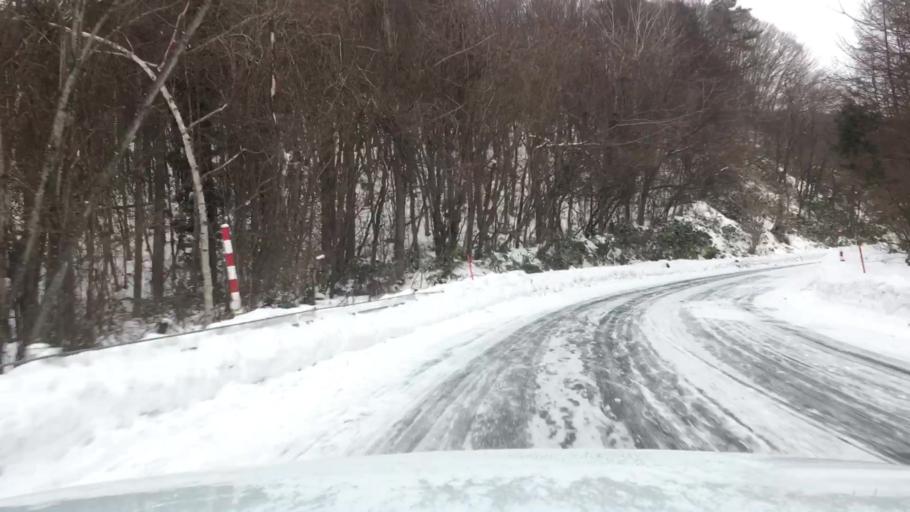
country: JP
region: Iwate
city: Shizukuishi
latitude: 39.9400
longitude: 140.9960
